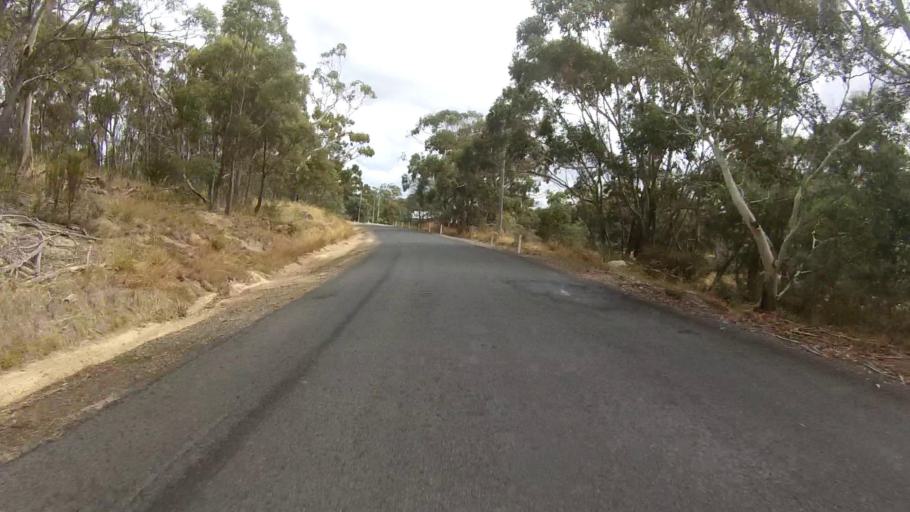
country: AU
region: Tasmania
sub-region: Break O'Day
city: St Helens
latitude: -41.8212
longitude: 147.8977
